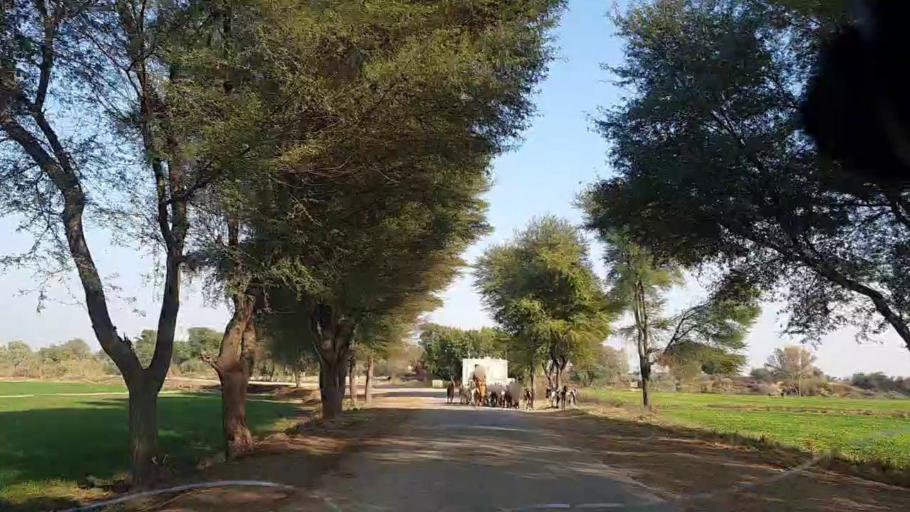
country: PK
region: Sindh
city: Khanpur
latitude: 27.6863
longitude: 69.4966
